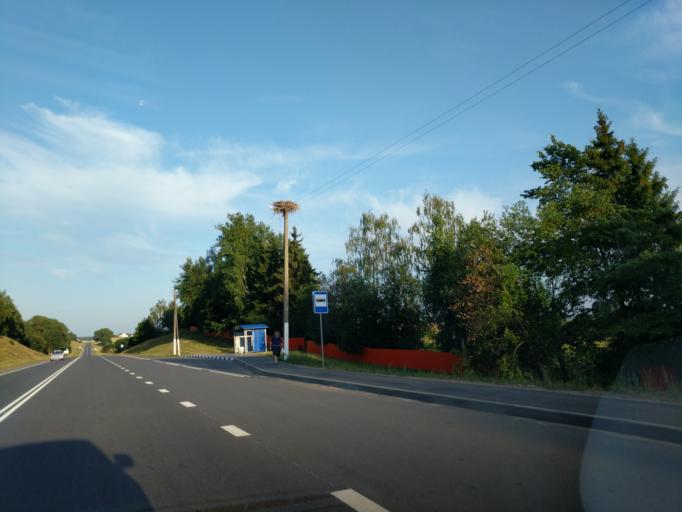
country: BY
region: Minsk
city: Syomkava
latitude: 54.1077
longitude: 27.4623
